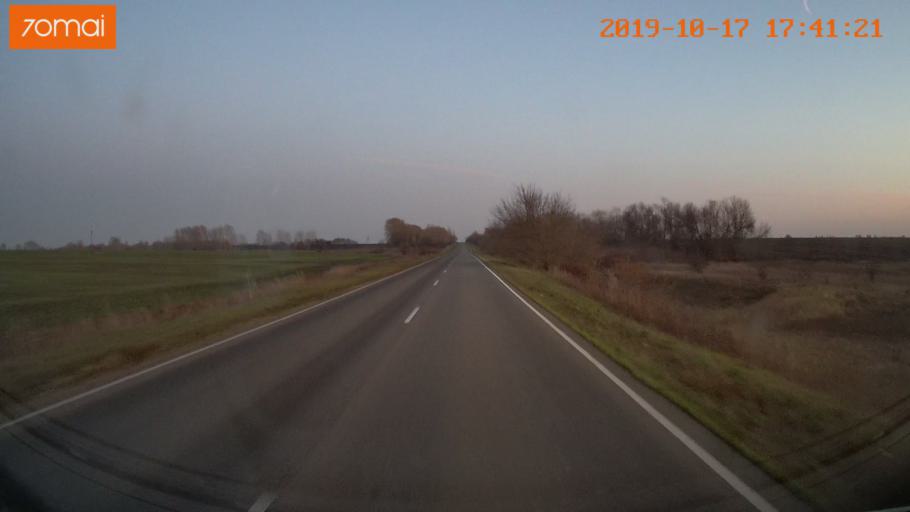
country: RU
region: Tula
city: Yepifan'
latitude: 53.7846
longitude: 38.6268
